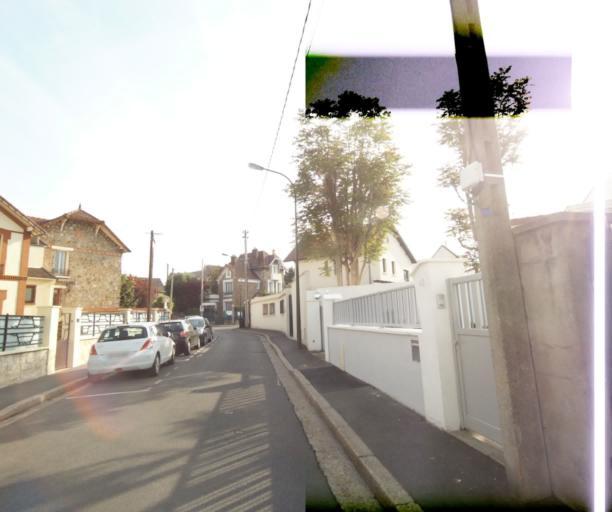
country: FR
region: Ile-de-France
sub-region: Departement du Val-d'Oise
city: Argenteuil
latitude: 48.9519
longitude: 2.2605
